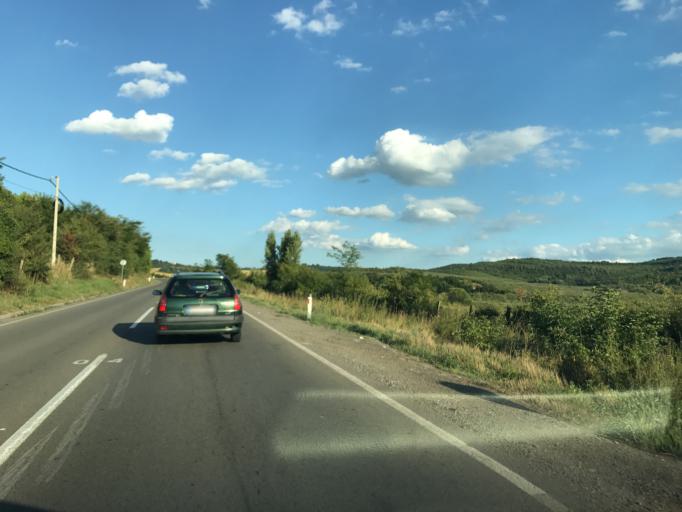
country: RS
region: Central Serbia
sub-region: Belgrade
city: Grocka
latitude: 44.7209
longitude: 20.6356
